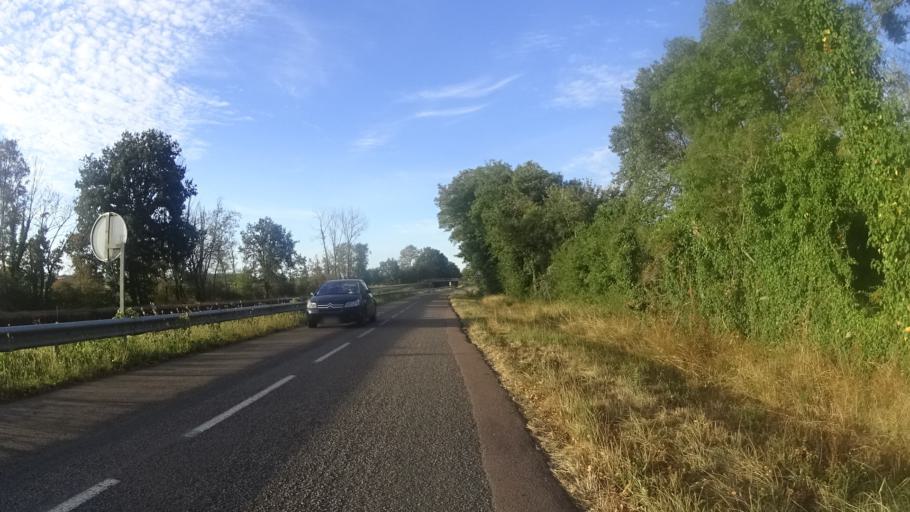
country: FR
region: Bourgogne
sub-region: Departement de Saone-et-Loire
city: Palinges
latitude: 46.5180
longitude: 4.1958
